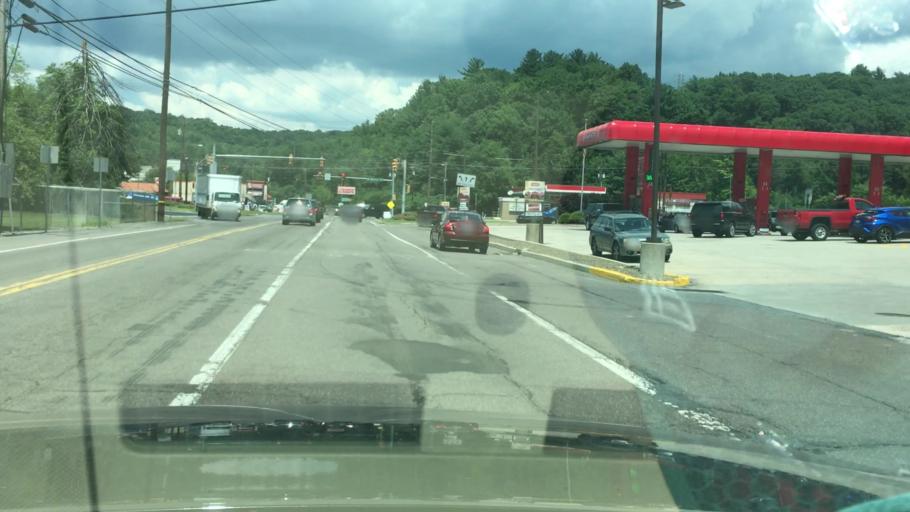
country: US
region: Pennsylvania
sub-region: Schuylkill County
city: Minersville
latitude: 40.6720
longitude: -76.2353
